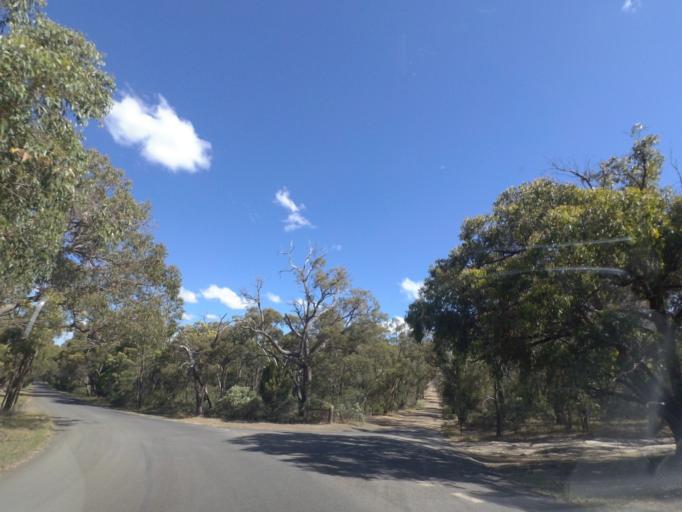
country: AU
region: Victoria
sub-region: Hume
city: Sunbury
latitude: -37.4422
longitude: 144.6645
